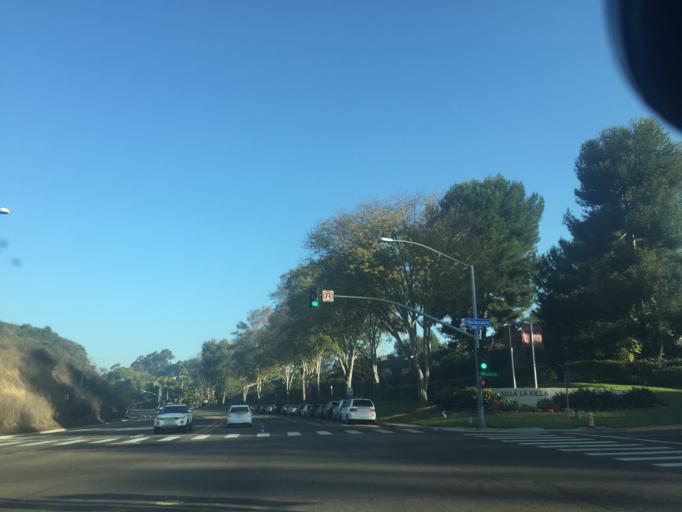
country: US
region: California
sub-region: San Diego County
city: La Jolla
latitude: 32.8621
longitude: -117.2363
